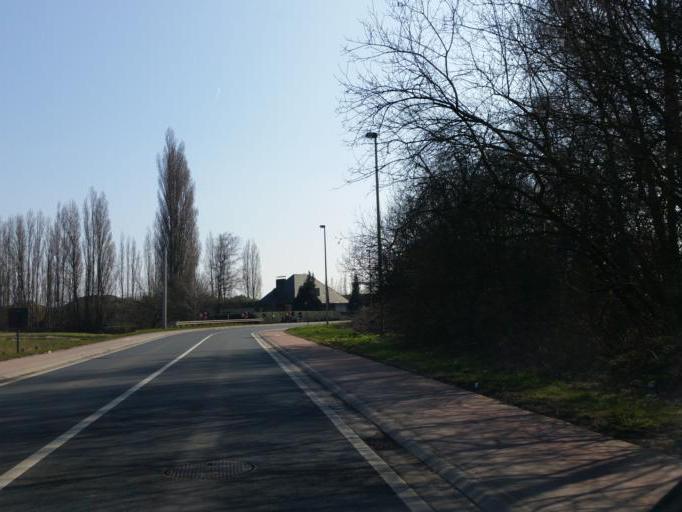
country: BE
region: Flanders
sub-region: Provincie Oost-Vlaanderen
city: Kruibeke
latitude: 51.1909
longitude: 4.3238
